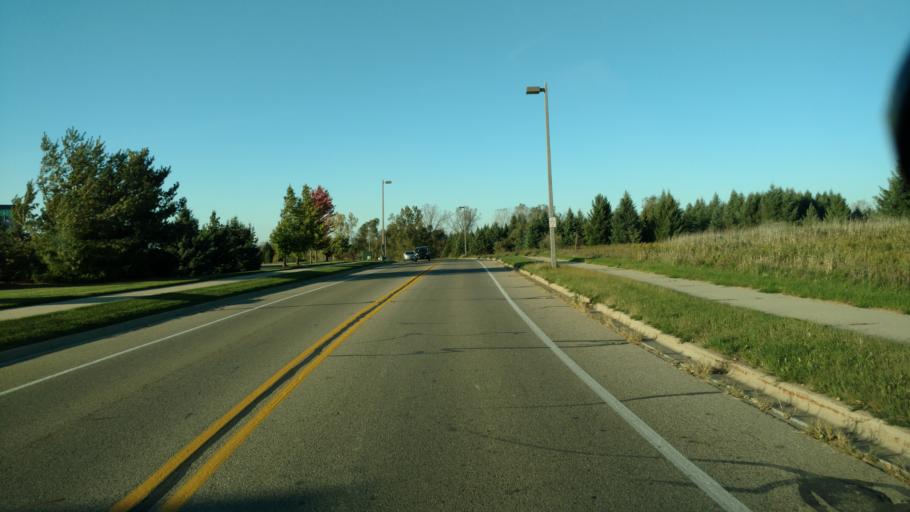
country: US
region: Michigan
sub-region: Ingham County
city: East Lansing
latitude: 42.7790
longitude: -84.5074
